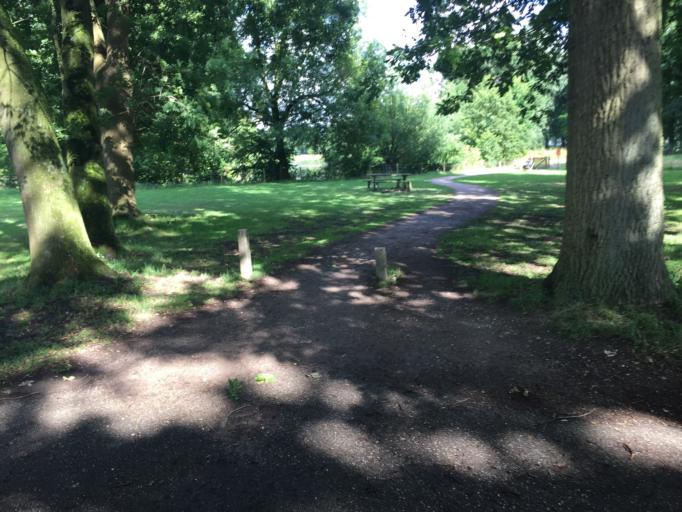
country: NL
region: Utrecht
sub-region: Gemeente Bunnik
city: Bunnik
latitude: 52.0730
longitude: 5.1742
